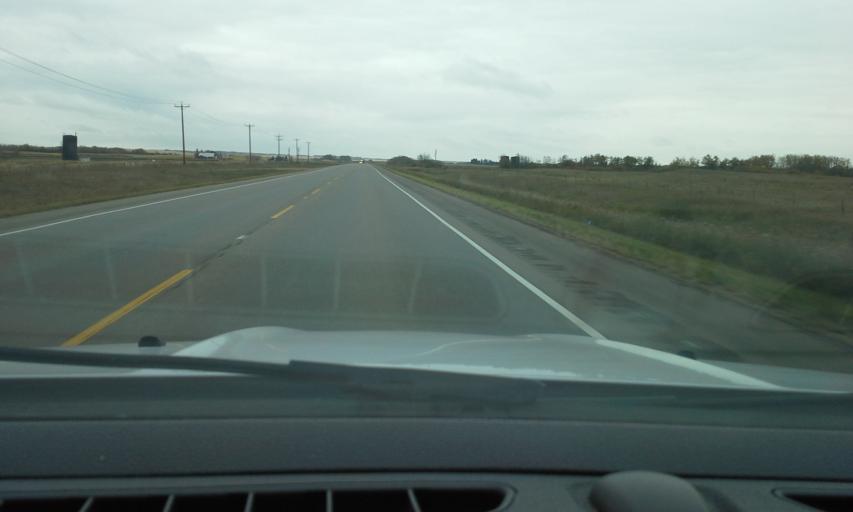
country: CA
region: Saskatchewan
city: Lloydminster
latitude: 53.2780
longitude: -109.8153
